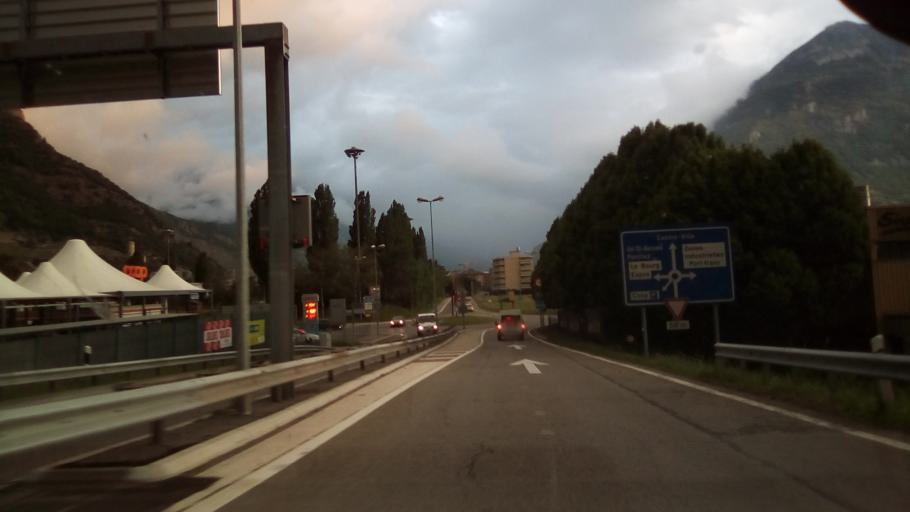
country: CH
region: Valais
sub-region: Martigny District
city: Martigny-Ville
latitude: 46.0989
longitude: 7.0838
